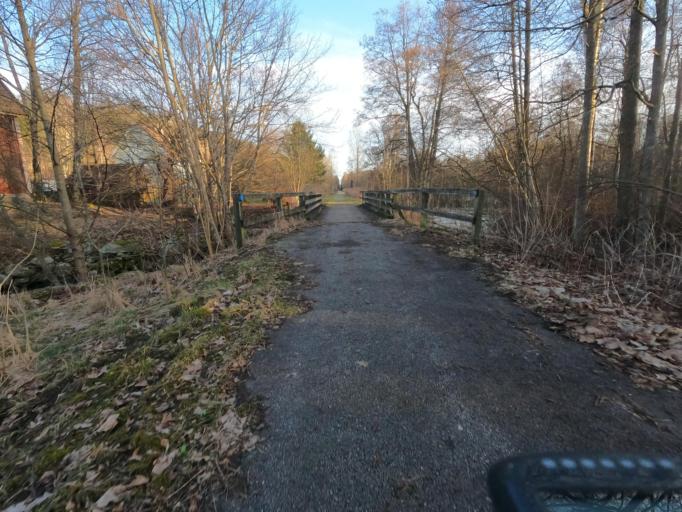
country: SE
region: Blekinge
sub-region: Karlshamns Kommun
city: Svangsta
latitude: 56.3701
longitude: 14.6837
